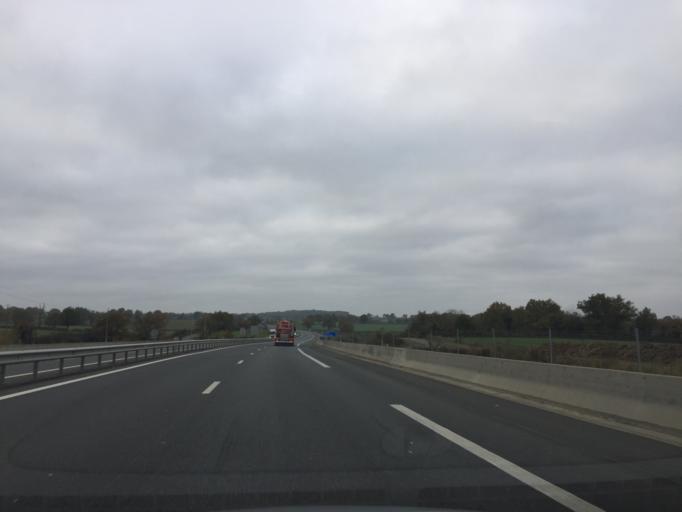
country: FR
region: Auvergne
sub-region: Departement de l'Allier
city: Desertines
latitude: 46.3817
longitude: 2.6875
